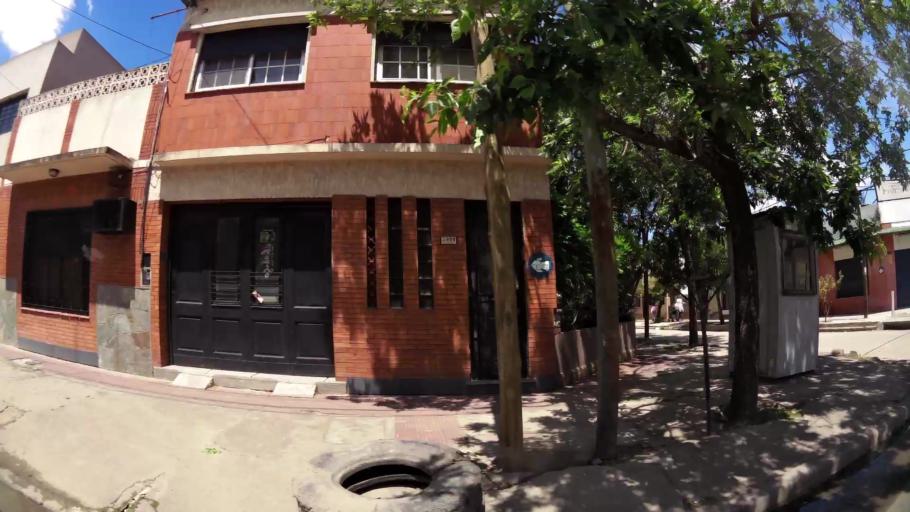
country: AR
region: Buenos Aires
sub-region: Partido de Lanus
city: Lanus
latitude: -34.7253
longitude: -58.4125
